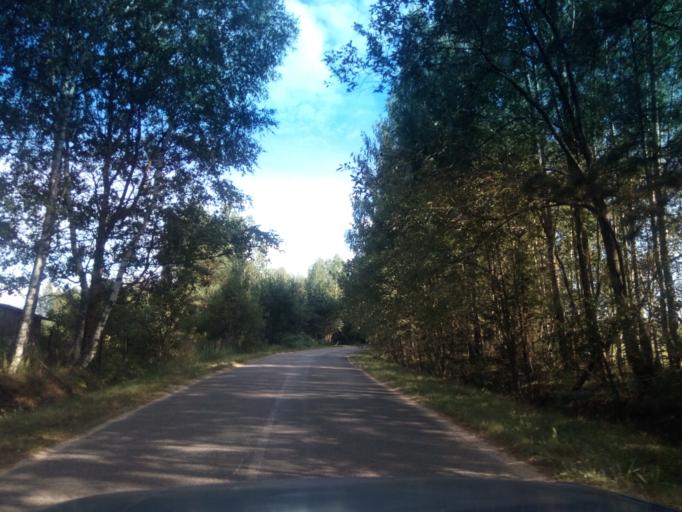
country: BY
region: Vitebsk
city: Polatsk
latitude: 55.4121
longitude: 28.7534
